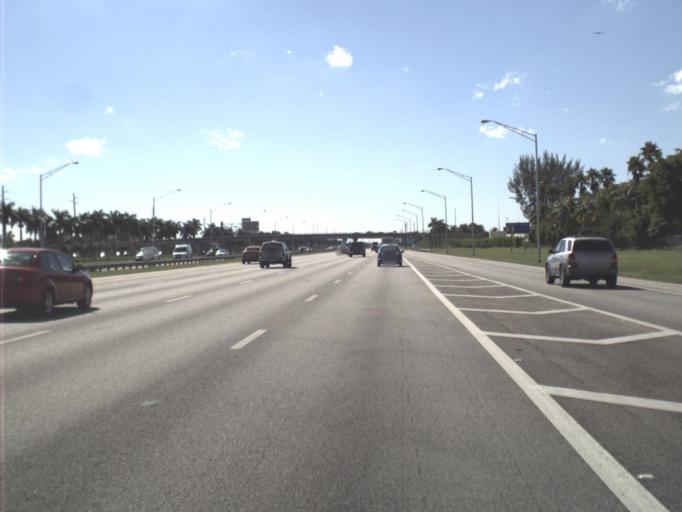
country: US
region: Florida
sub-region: Miami-Dade County
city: Tamiami
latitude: 25.7507
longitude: -80.3851
